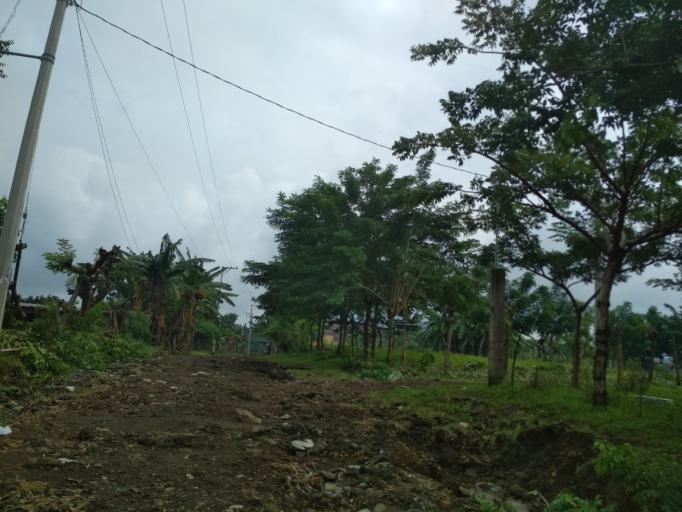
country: MX
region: Veracruz
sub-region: San Andres Tuxtla
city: Matacapan
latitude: 18.4408
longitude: -95.1491
